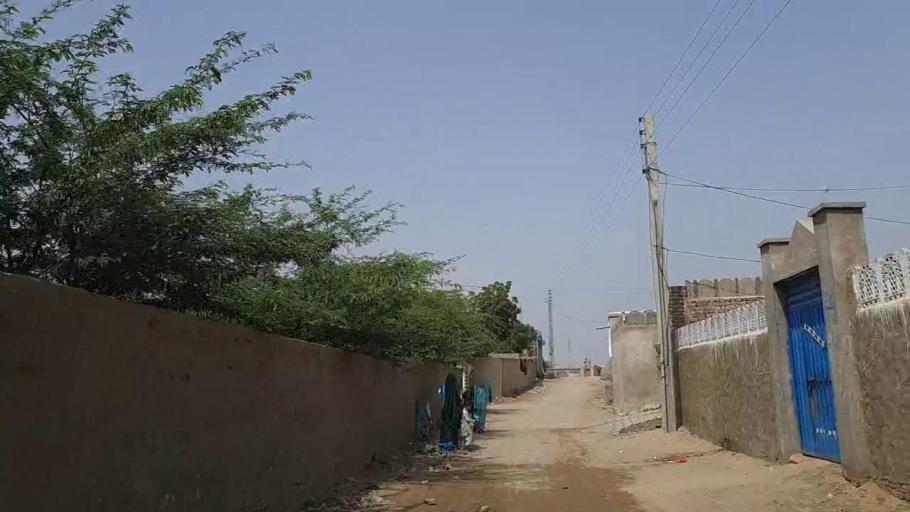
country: PK
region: Sindh
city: Mithi
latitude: 24.7284
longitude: 69.8057
